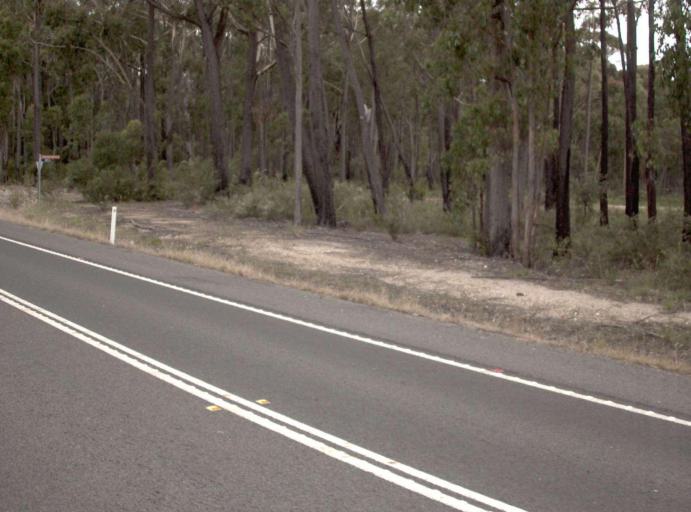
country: AU
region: Victoria
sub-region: East Gippsland
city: Lakes Entrance
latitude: -37.7292
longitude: 147.9461
